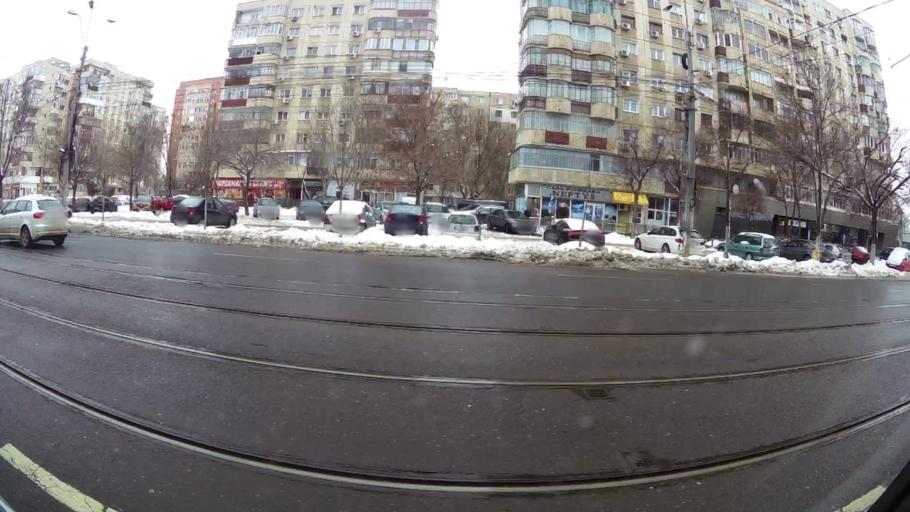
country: RO
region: Ilfov
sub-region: Comuna Popesti-Leordeni
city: Popesti-Leordeni
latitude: 44.3898
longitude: 26.1309
